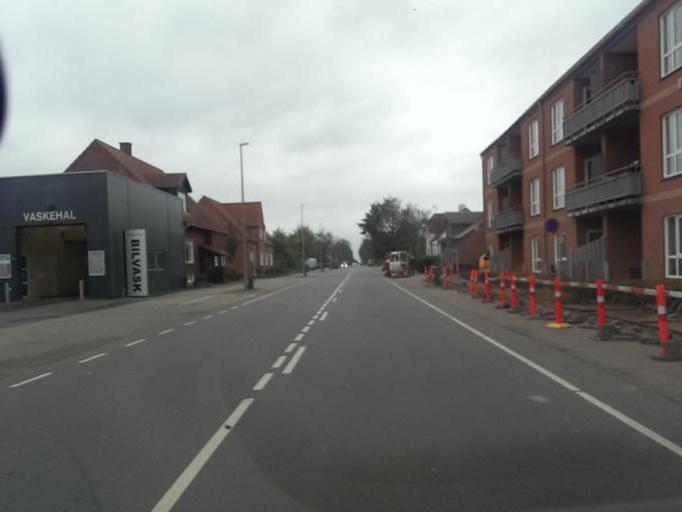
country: DK
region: South Denmark
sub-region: Esbjerg Kommune
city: Bramming
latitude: 55.4637
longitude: 8.7038
